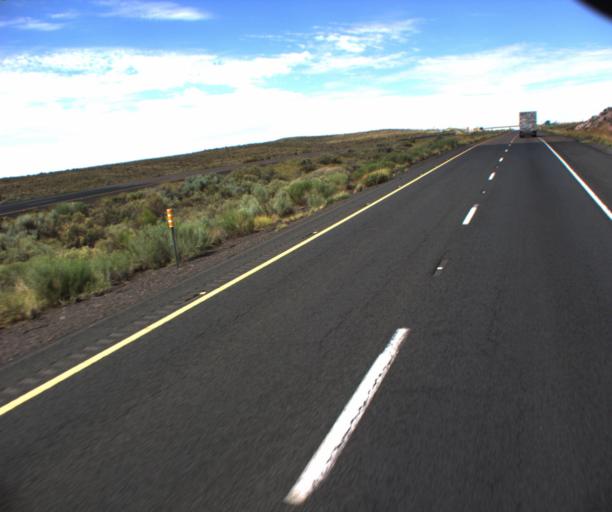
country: US
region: Arizona
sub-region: Apache County
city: Houck
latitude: 35.1010
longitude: -109.6320
